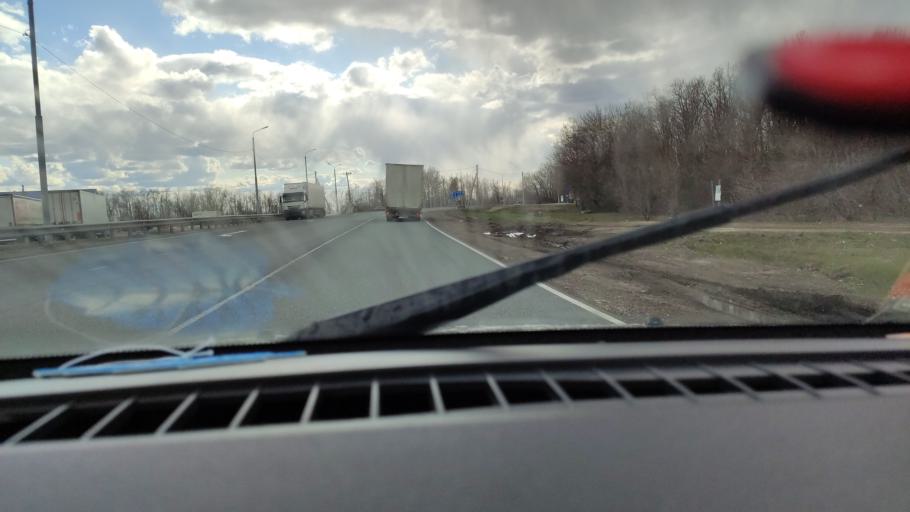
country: RU
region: Saratov
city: Balakovo
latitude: 52.0962
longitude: 47.7256
